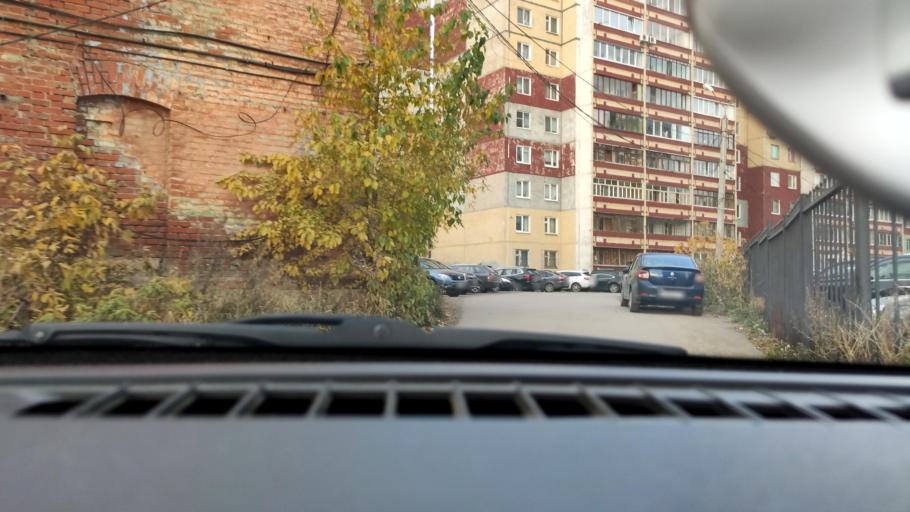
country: RU
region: Perm
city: Perm
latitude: 57.9959
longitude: 56.2671
